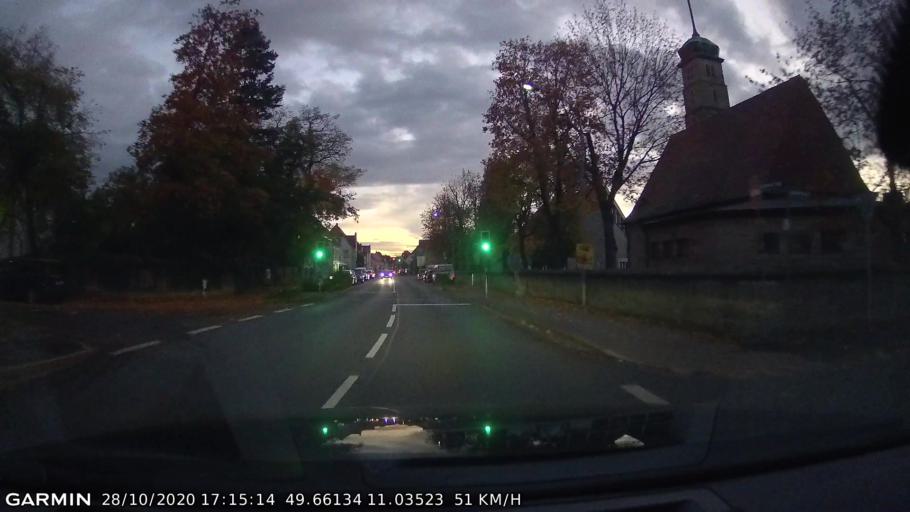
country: DE
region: Bavaria
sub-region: Regierungsbezirk Mittelfranken
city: Baiersdorf
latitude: 49.6613
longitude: 11.0352
